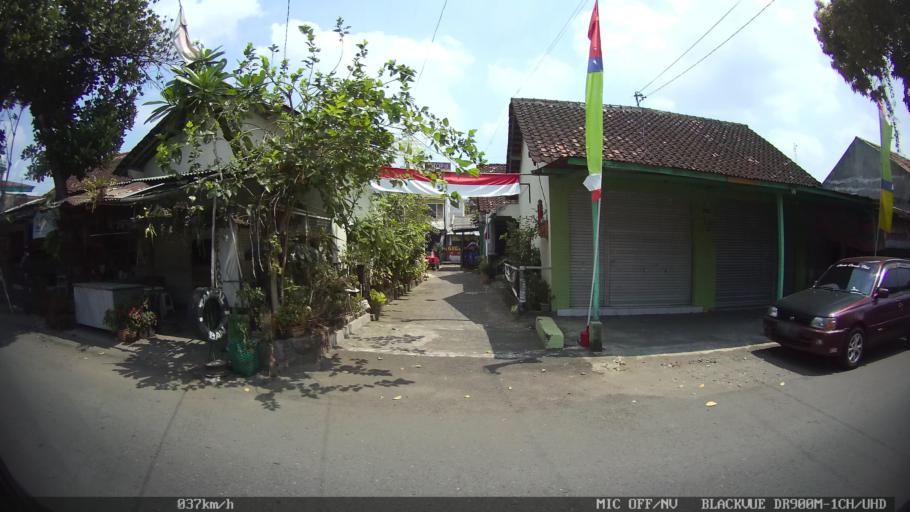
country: ID
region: Daerah Istimewa Yogyakarta
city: Yogyakarta
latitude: -7.8092
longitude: 110.3979
